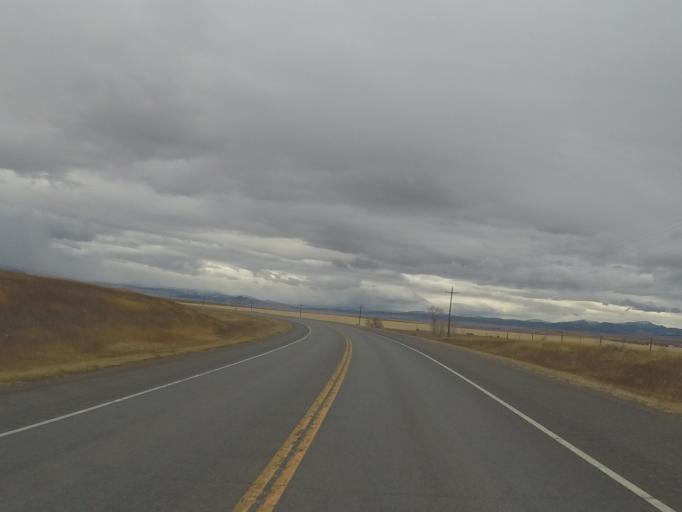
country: US
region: Montana
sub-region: Lewis and Clark County
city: East Helena
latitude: 46.5602
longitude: -111.7794
